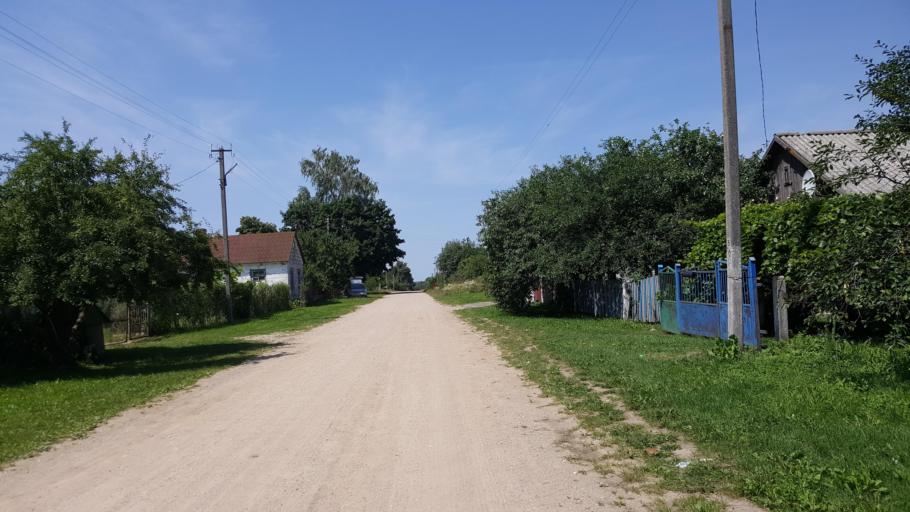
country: BY
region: Brest
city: Vysokaye
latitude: 52.3521
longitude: 23.4489
